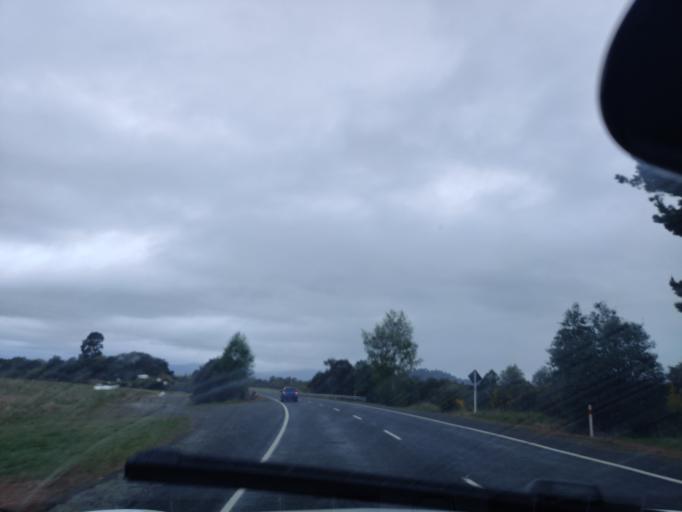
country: NZ
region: Waikato
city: Turangi
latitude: -38.9781
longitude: 175.7730
